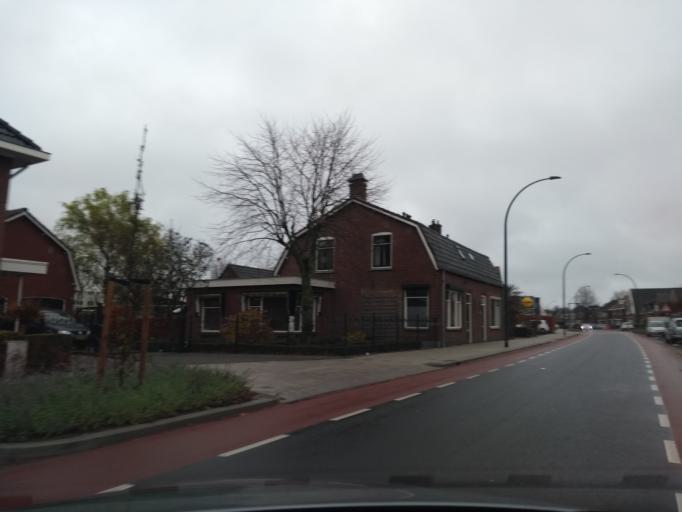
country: NL
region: Overijssel
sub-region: Gemeente Wierden
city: Wierden
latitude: 52.3595
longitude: 6.5845
